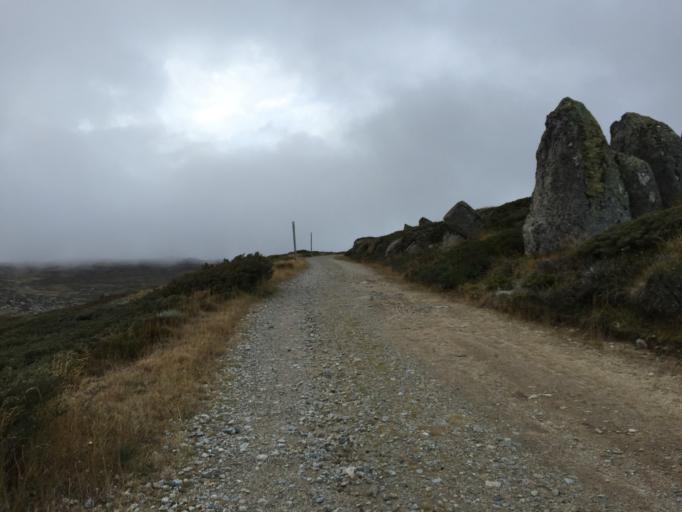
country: AU
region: New South Wales
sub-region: Snowy River
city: Jindabyne
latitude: -36.4560
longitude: 148.3016
